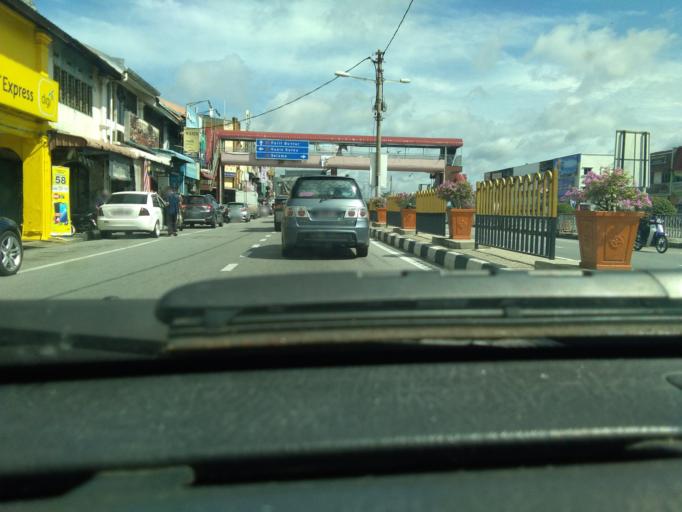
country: MY
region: Perak
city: Bagan Serai
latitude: 5.0116
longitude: 100.5346
